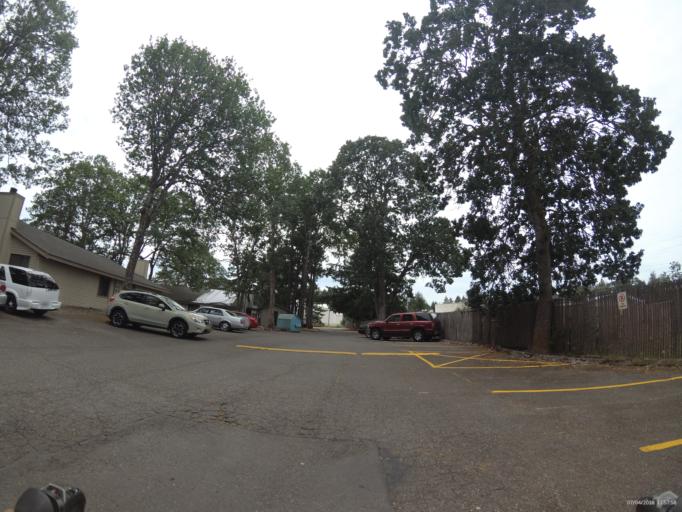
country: US
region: Washington
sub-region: Pierce County
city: McChord Air Force Base
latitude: 47.1403
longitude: -122.4980
